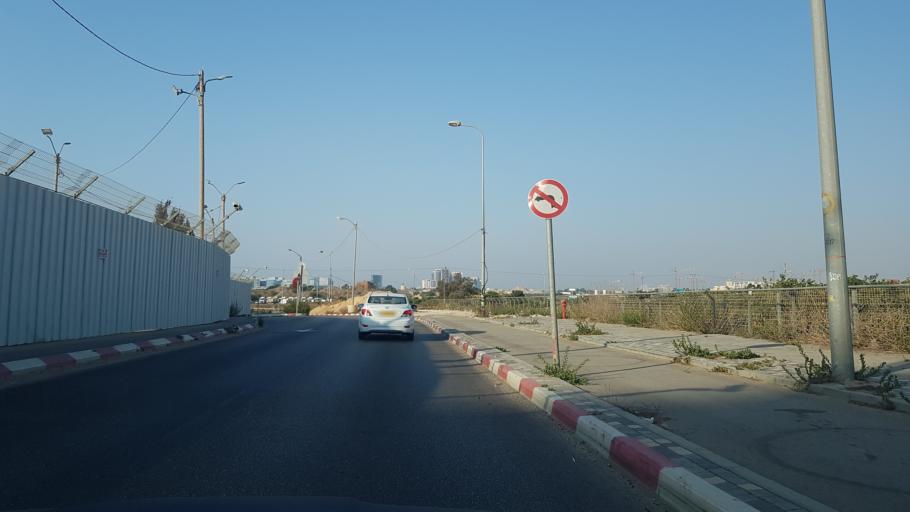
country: IL
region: Tel Aviv
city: Herzliyya
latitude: 32.1445
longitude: 34.8069
